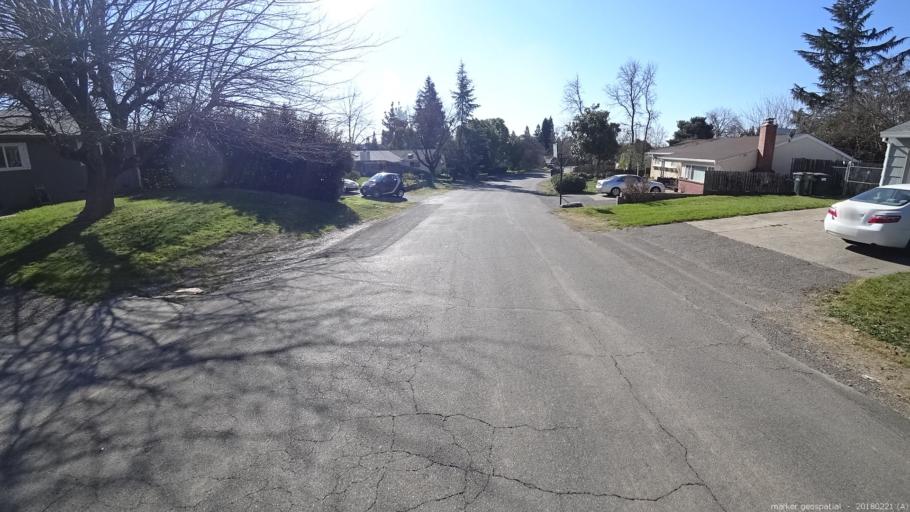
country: US
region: California
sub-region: Sacramento County
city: Orangevale
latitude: 38.6871
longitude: -121.2423
